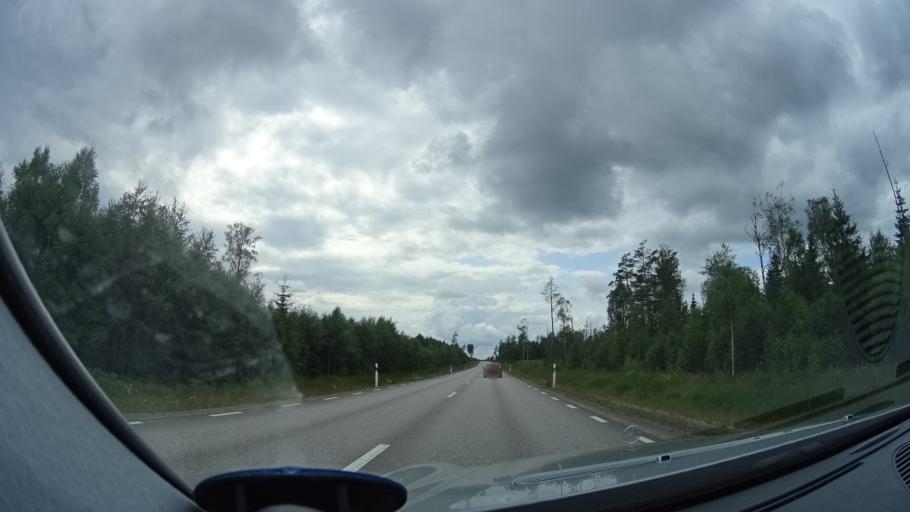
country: SE
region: Kronoberg
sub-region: Tingsryds Kommun
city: Tingsryd
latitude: 56.5105
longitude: 15.0147
